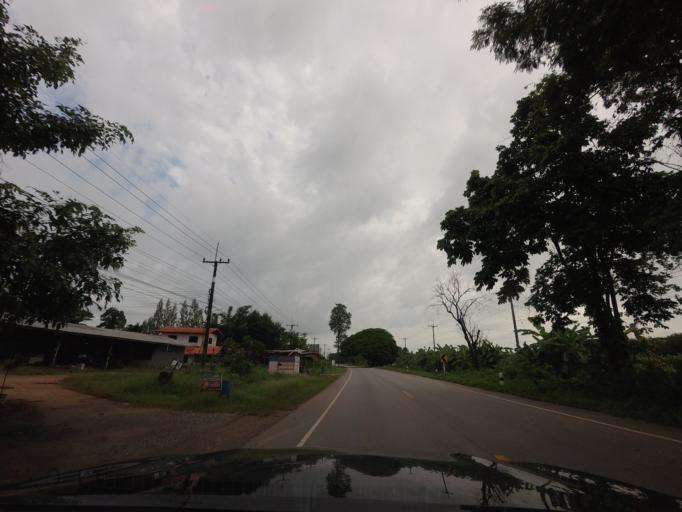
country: TH
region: Changwat Udon Thani
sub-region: Amphoe Ban Phue
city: Ban Phue
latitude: 17.7238
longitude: 102.3941
